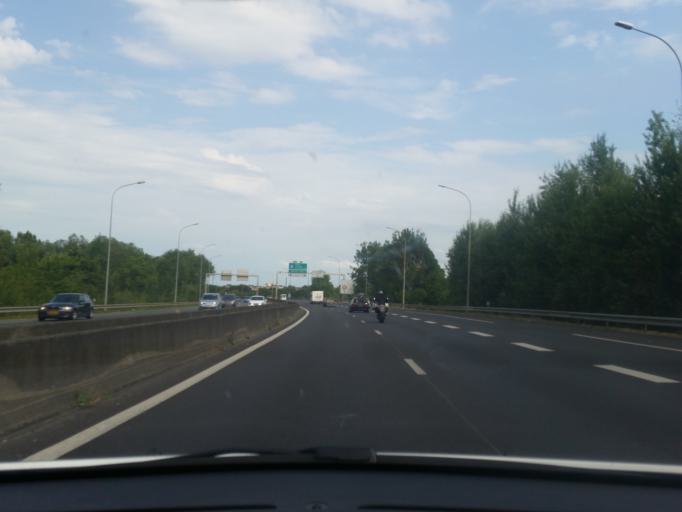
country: FR
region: Pays de la Loire
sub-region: Departement de Maine-et-Loire
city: Angers
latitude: 47.4664
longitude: -0.5822
